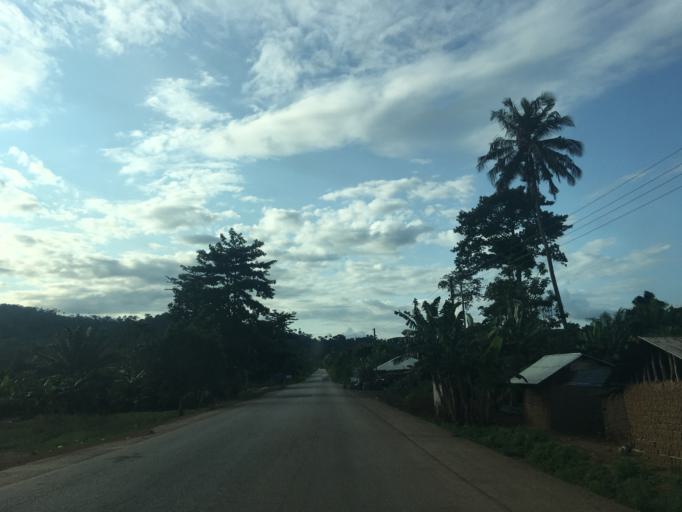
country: GH
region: Western
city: Bibiani
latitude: 6.2561
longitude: -2.2247
